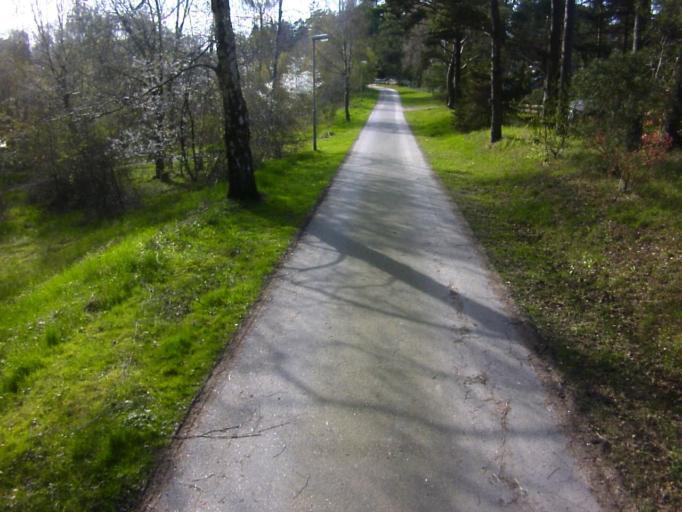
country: SE
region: Skane
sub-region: Kavlinge Kommun
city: Hofterup
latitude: 55.8242
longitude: 12.9399
